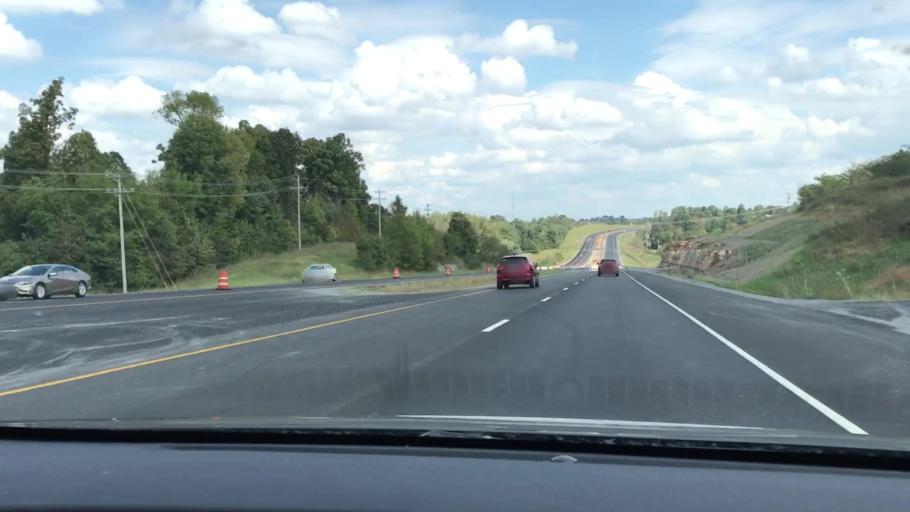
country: US
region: Kentucky
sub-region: Trigg County
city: Cadiz
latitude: 36.8498
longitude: -87.8190
